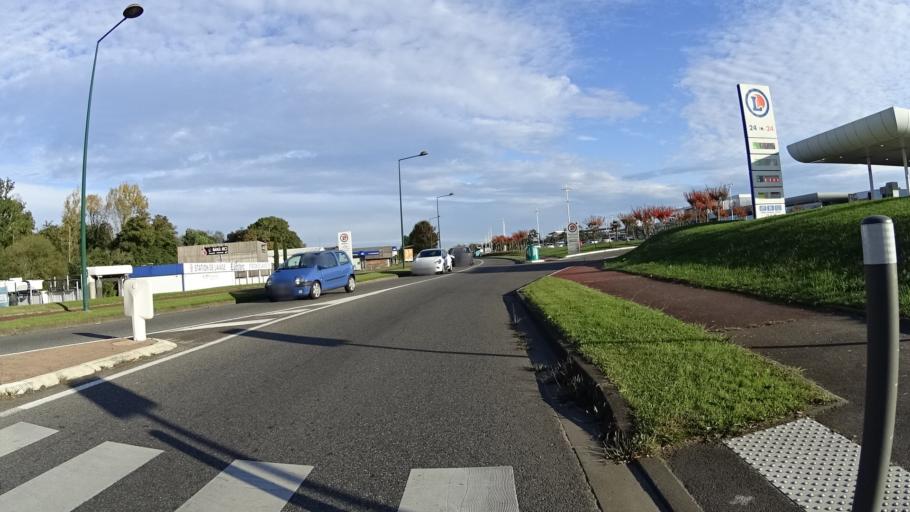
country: FR
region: Aquitaine
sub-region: Departement des Landes
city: Saint-Paul-les-Dax
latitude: 43.7327
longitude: -1.0444
